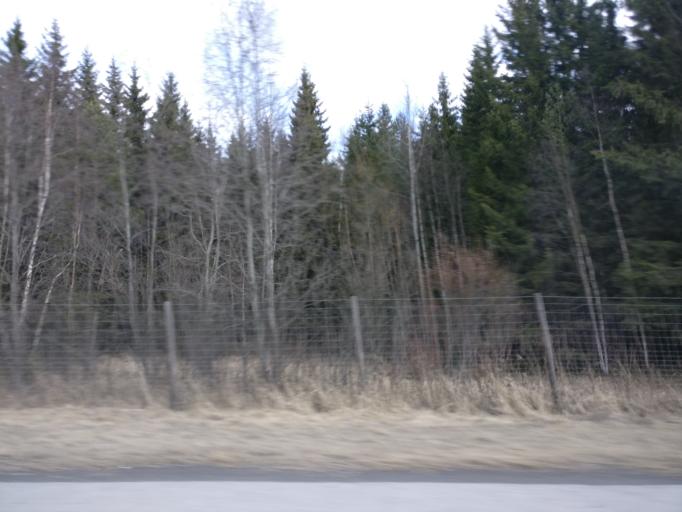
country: FI
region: Haeme
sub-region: Haemeenlinna
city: Tervakoski
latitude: 60.8323
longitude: 24.6553
